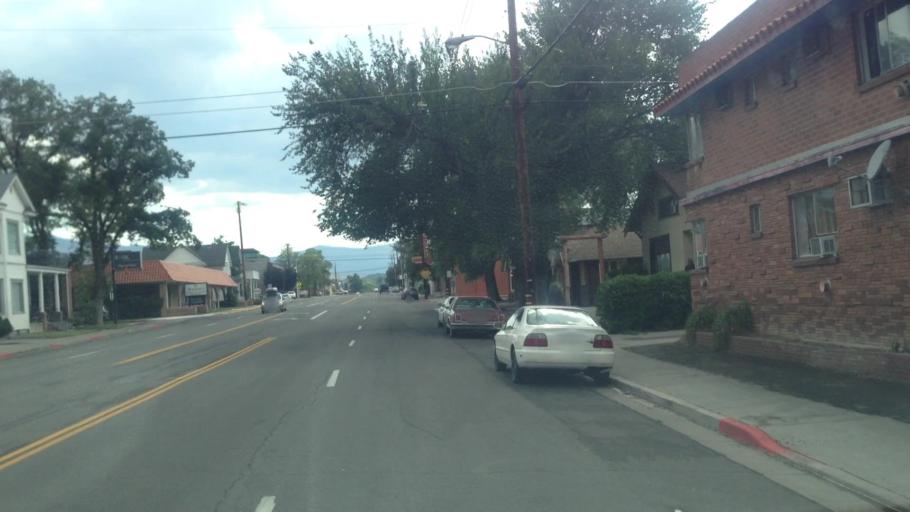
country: US
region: Nevada
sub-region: Washoe County
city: Reno
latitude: 39.5257
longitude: -119.8203
